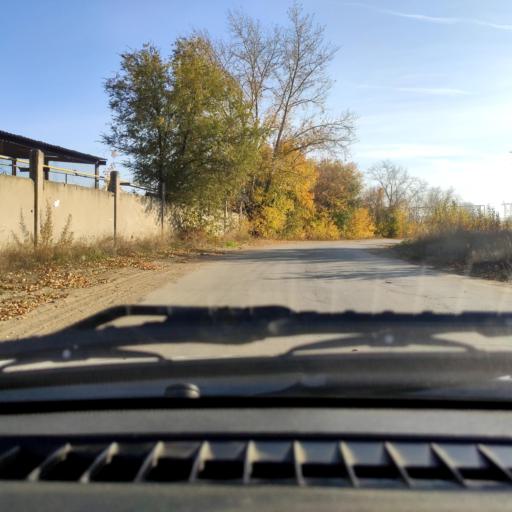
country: RU
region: Samara
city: Zhigulevsk
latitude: 53.4743
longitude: 49.5011
